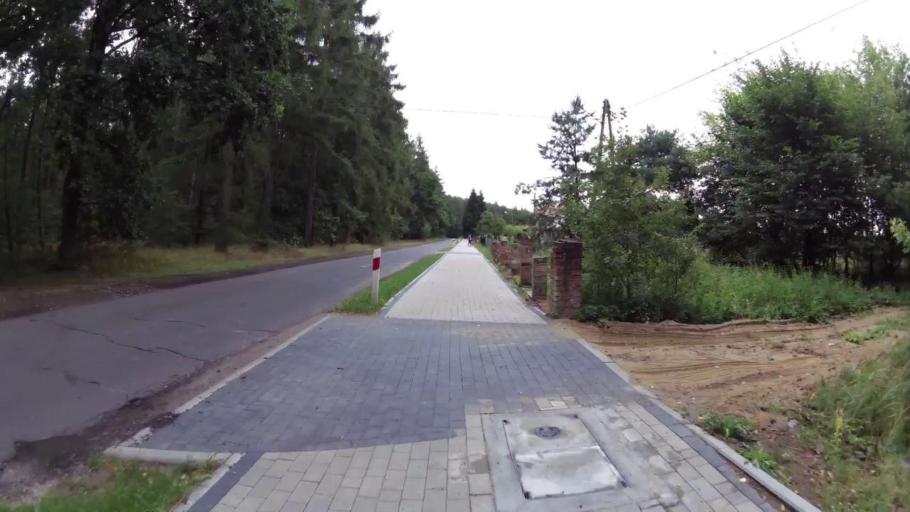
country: PL
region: West Pomeranian Voivodeship
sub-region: Powiat mysliborski
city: Debno
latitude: 52.7669
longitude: 14.6948
